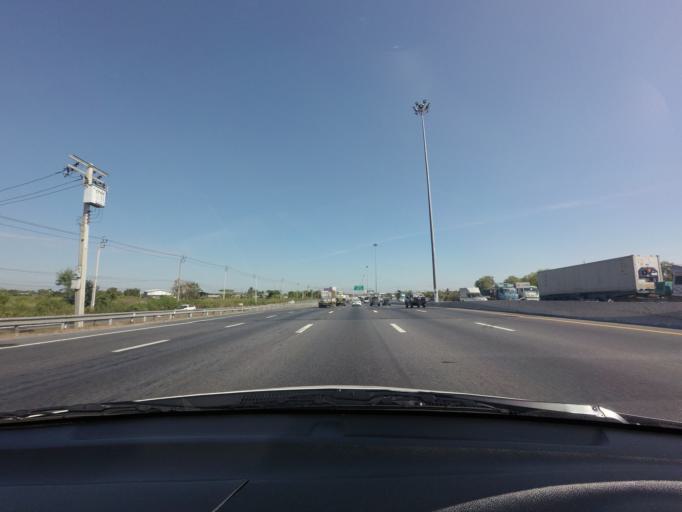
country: TH
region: Bangkok
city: Sai Mai
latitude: 13.9077
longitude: 100.6984
